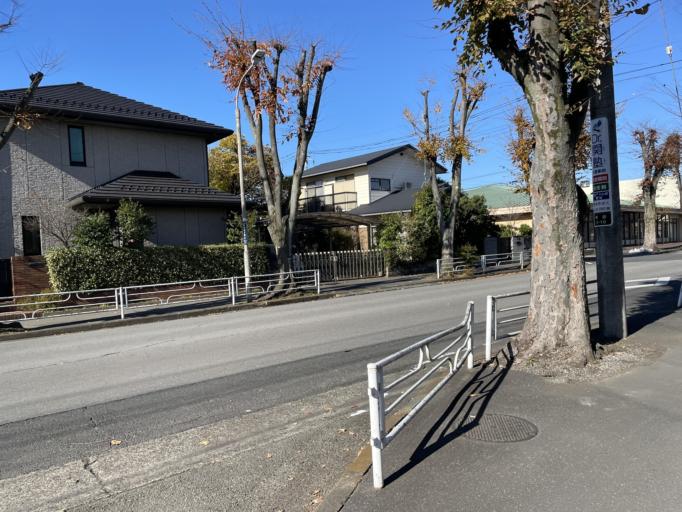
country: JP
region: Saitama
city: Satte
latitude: 36.0712
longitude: 139.7019
